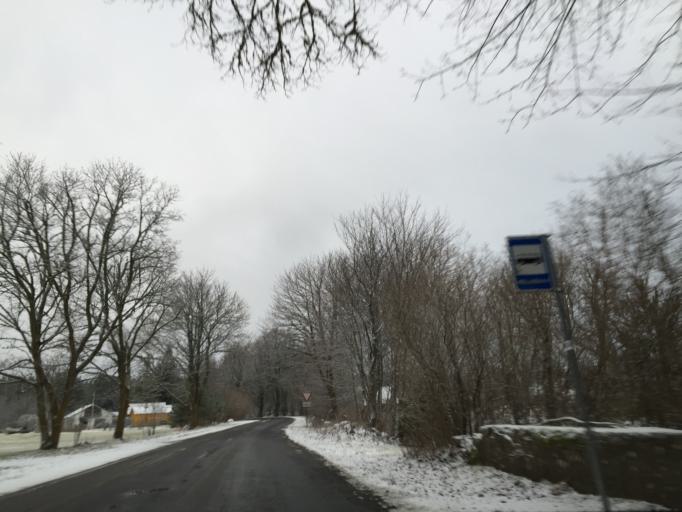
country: EE
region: Saare
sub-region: Orissaare vald
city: Orissaare
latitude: 58.6105
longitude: 23.3001
